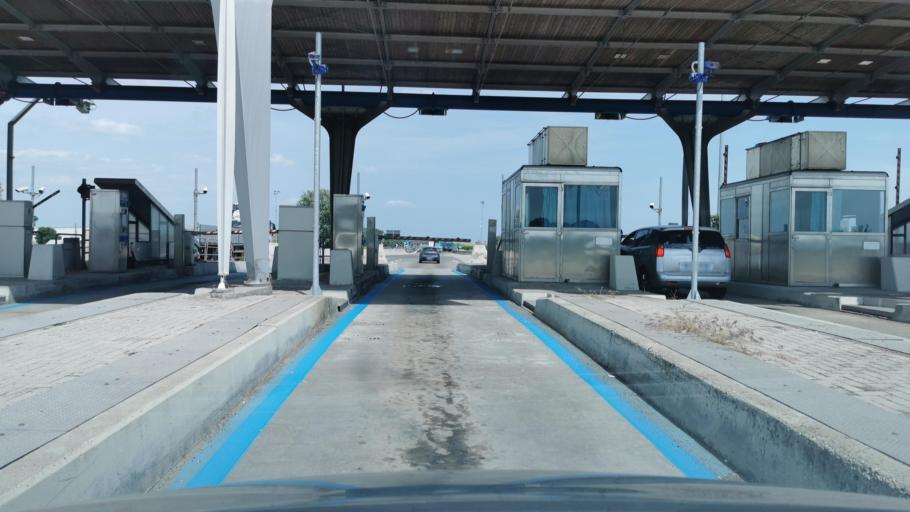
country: IT
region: Emilia-Romagna
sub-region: Provincia di Ravenna
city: Barbiano
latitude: 44.3870
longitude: 11.9084
